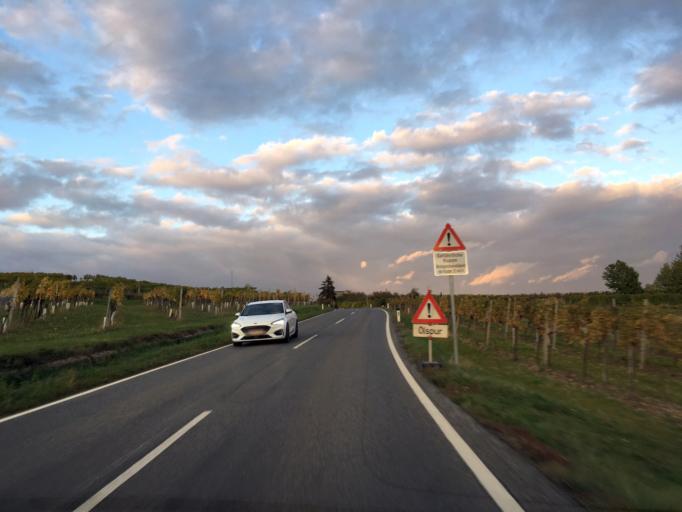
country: AT
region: Lower Austria
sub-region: Politischer Bezirk Baden
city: Pfaffstatten
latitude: 48.0261
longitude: 16.2600
